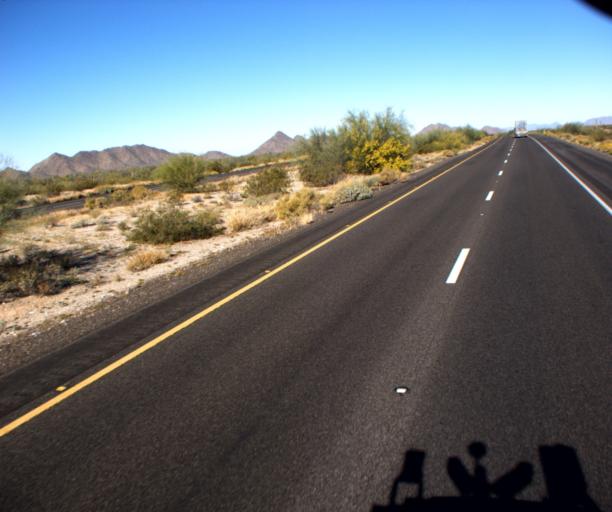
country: US
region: Arizona
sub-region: Maricopa County
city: Gila Bend
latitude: 32.8837
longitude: -112.4635
